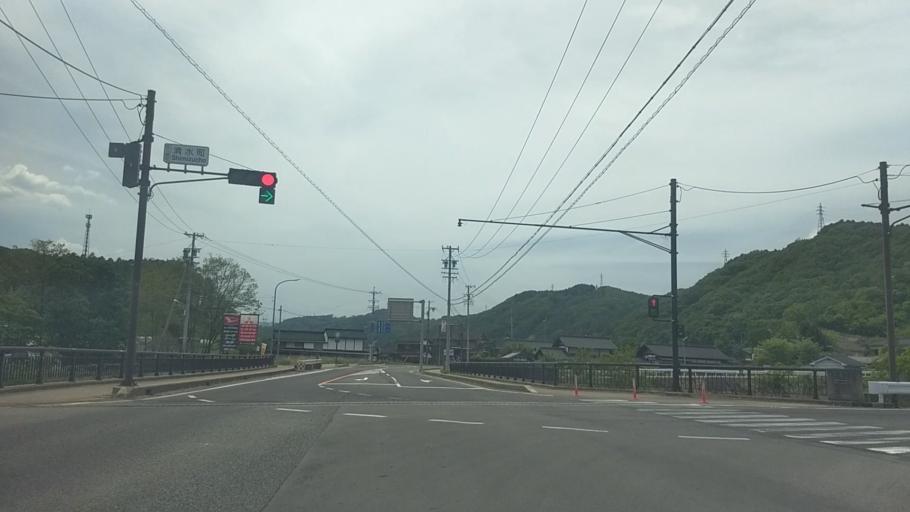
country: JP
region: Nagano
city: Saku
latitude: 36.1303
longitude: 138.4705
